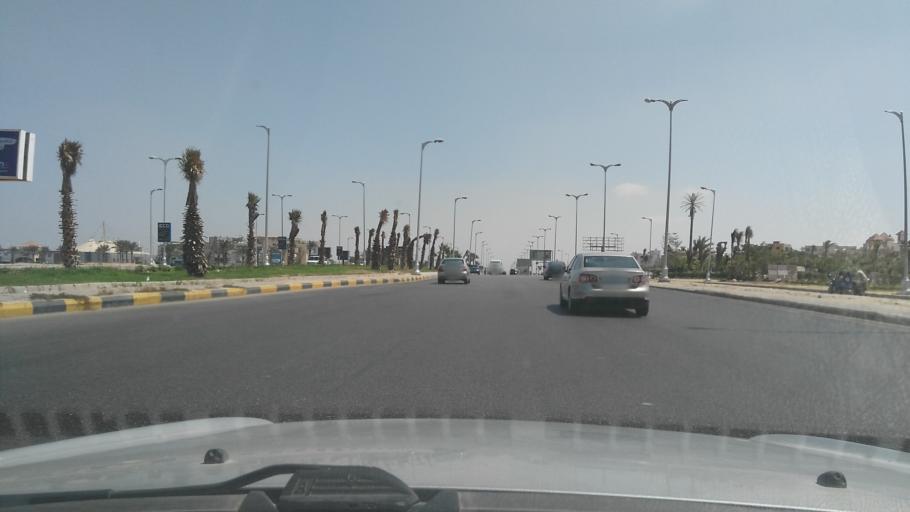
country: EG
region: Al Jizah
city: Madinat Sittah Uktubar
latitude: 30.0008
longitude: 30.9697
